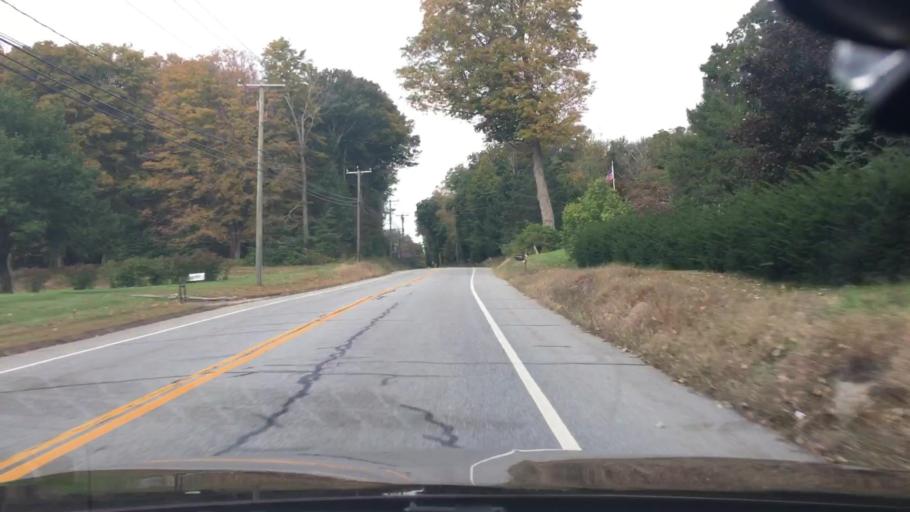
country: US
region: Connecticut
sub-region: Tolland County
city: Crystal Lake
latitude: 41.9760
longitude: -72.3775
